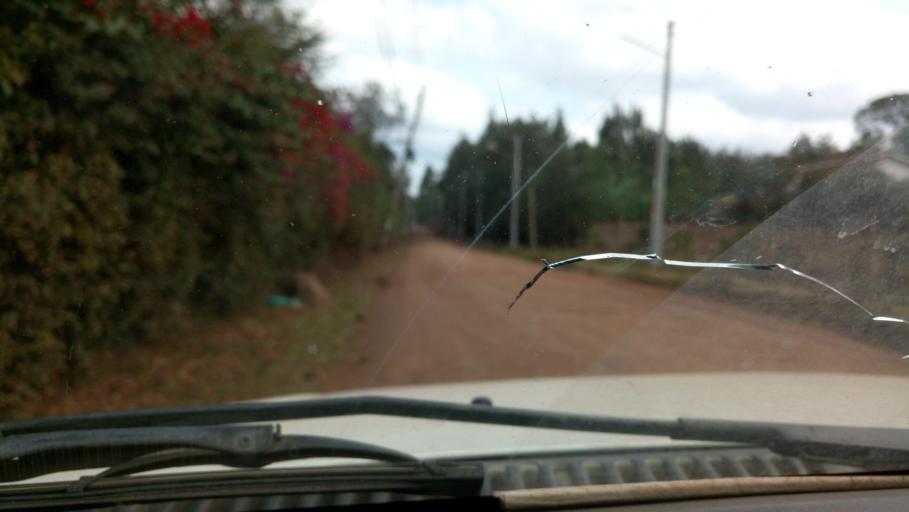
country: KE
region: Nairobi Area
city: Nairobi
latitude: -1.3363
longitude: 36.7479
